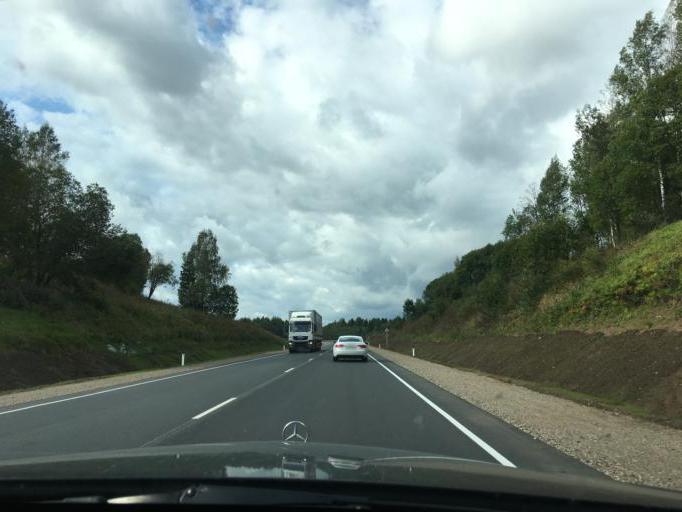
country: RU
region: Tverskaya
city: Toropets
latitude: 56.3309
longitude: 31.2317
